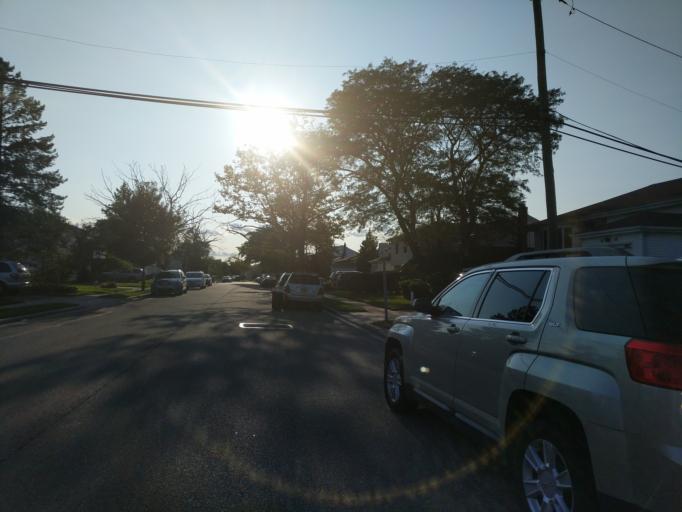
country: US
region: New York
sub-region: Nassau County
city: South Valley Stream
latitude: 40.6494
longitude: -73.7330
